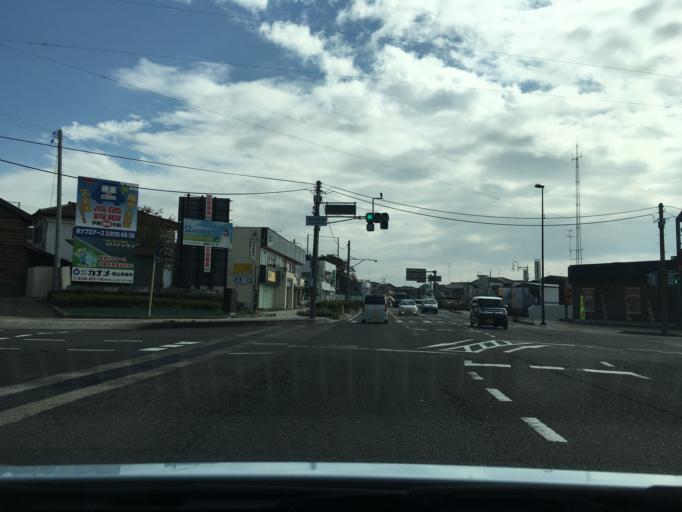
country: JP
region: Fukushima
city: Koriyama
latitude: 37.3842
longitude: 140.3602
